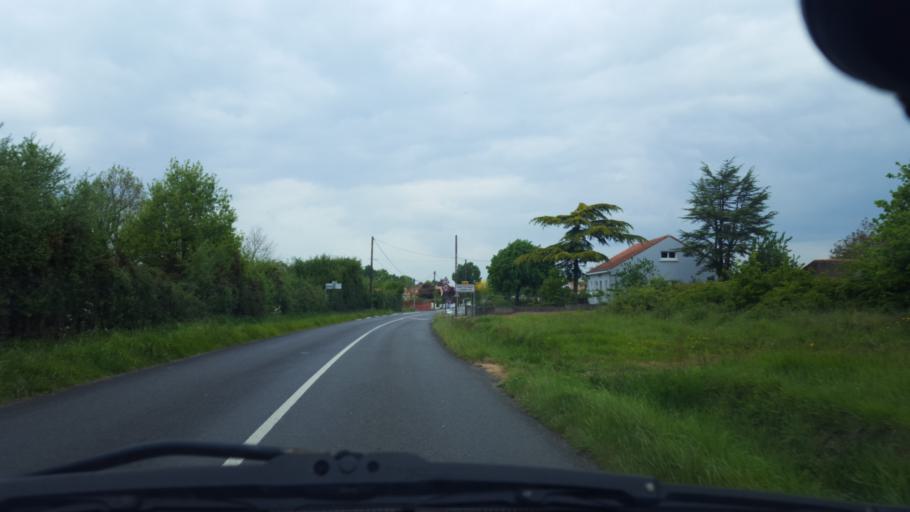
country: FR
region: Pays de la Loire
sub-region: Departement de la Loire-Atlantique
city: Saint-Philbert-de-Grand-Lieu
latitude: 47.0245
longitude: -1.6339
